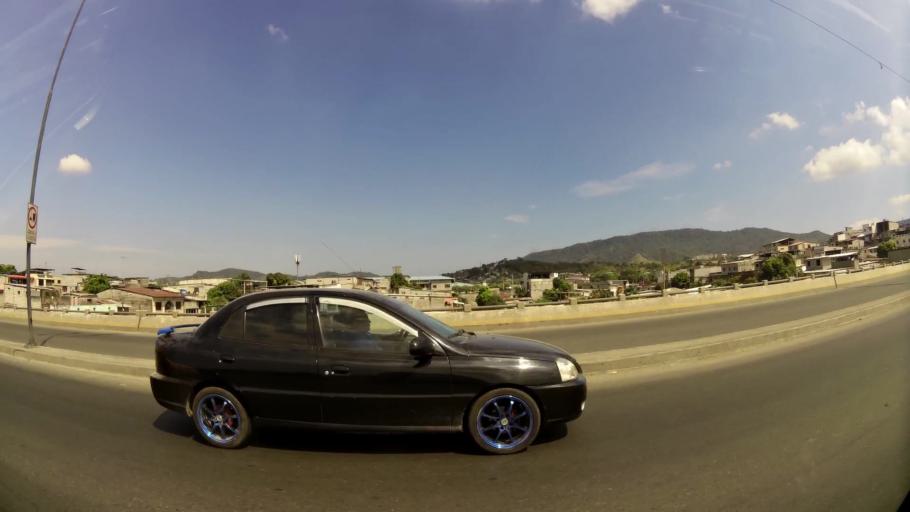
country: EC
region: Guayas
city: Santa Lucia
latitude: -2.1392
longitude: -79.9414
